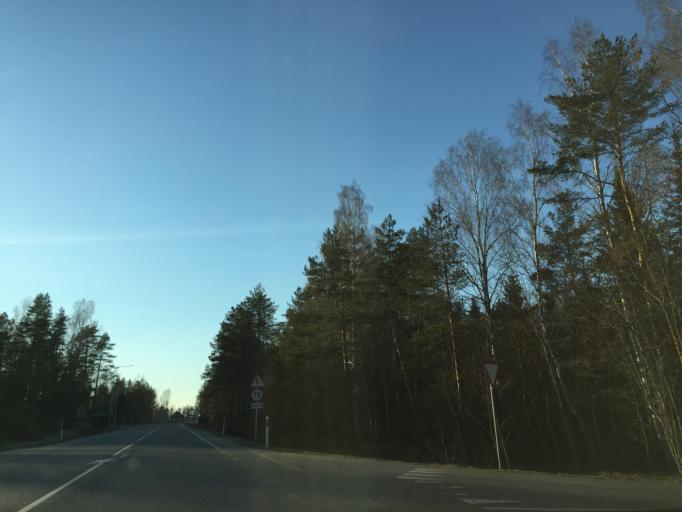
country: EE
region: Ida-Virumaa
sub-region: Johvi vald
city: Johvi
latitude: 59.2188
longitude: 27.5176
